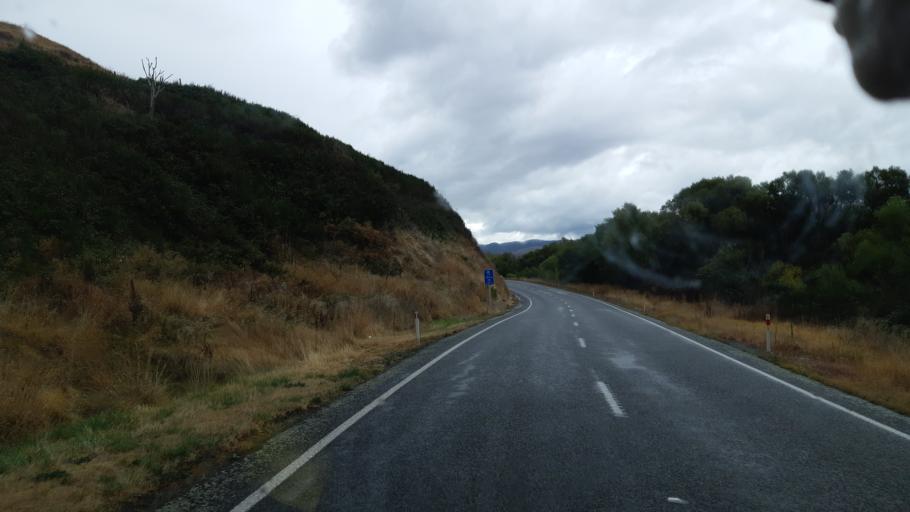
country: NZ
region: Canterbury
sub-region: Hurunui District
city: Amberley
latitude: -42.5786
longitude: 172.7546
